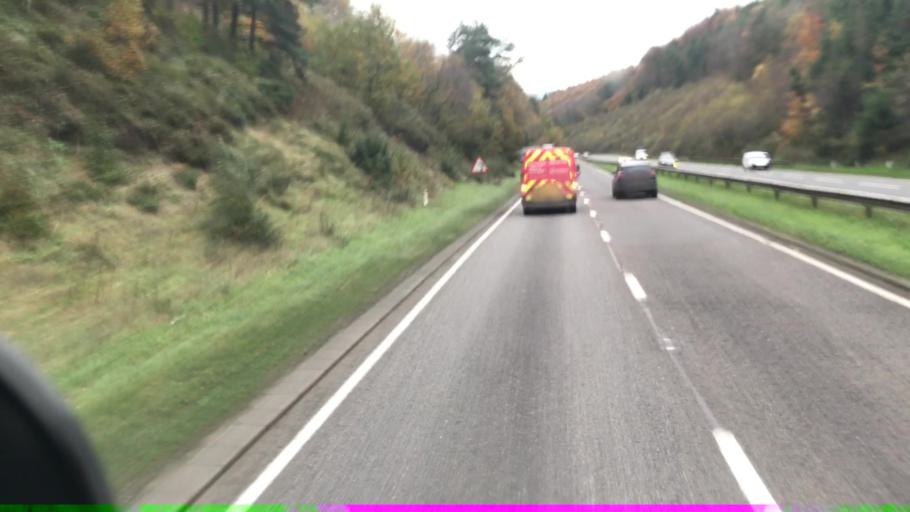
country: GB
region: England
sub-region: Devon
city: Chudleigh
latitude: 50.6456
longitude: -3.5544
